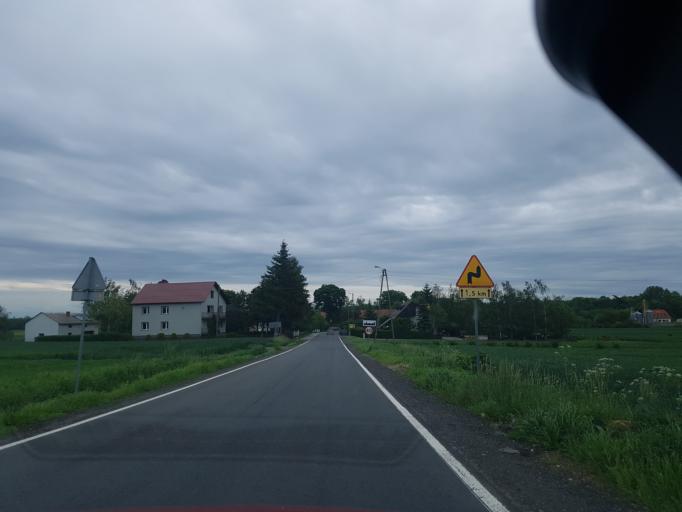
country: PL
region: Lower Silesian Voivodeship
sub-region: Powiat wroclawski
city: Katy Wroclawskie
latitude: 50.9826
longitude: 16.7434
